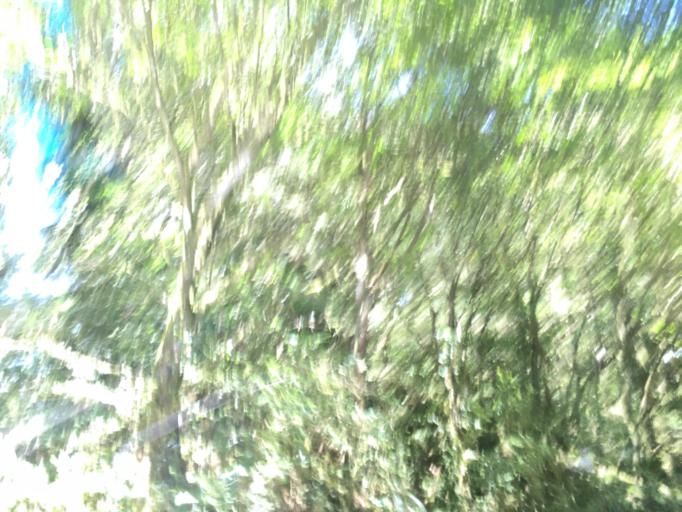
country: TW
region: Taiwan
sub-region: Yilan
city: Yilan
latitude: 24.6174
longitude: 121.4684
